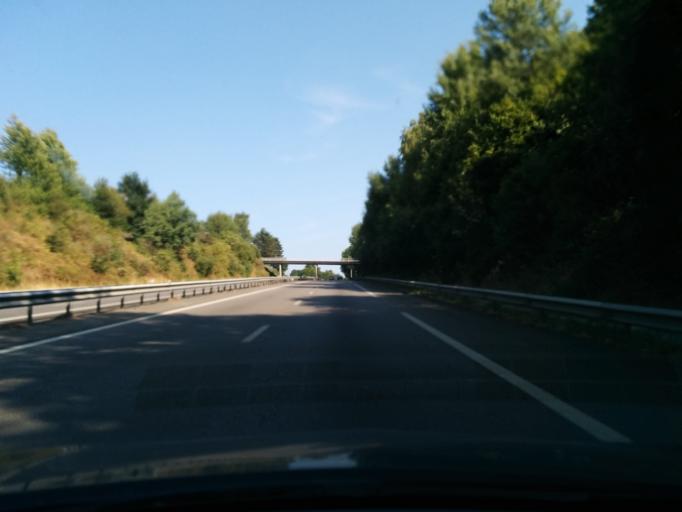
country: FR
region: Limousin
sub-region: Departement de la Haute-Vienne
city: Boisseuil
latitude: 45.7682
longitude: 1.3209
